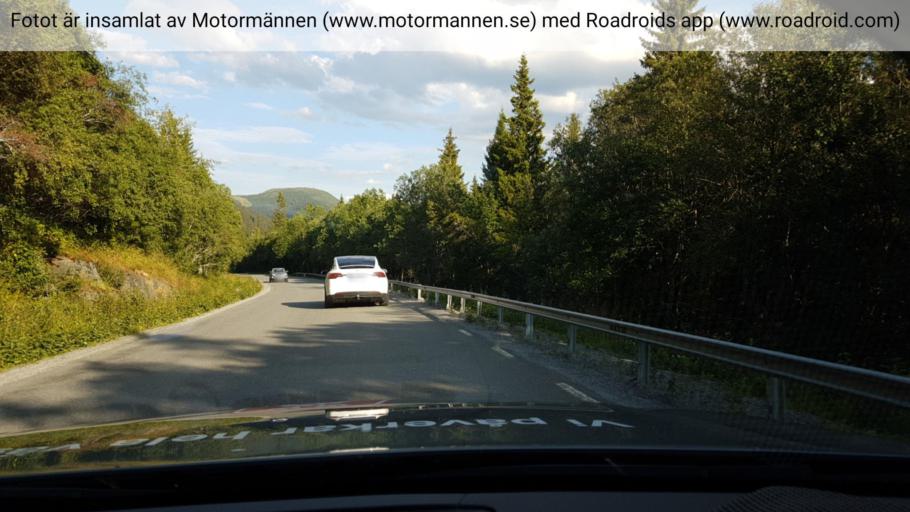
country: SE
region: Jaemtland
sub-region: Are Kommun
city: Are
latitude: 63.4110
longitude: 13.0401
